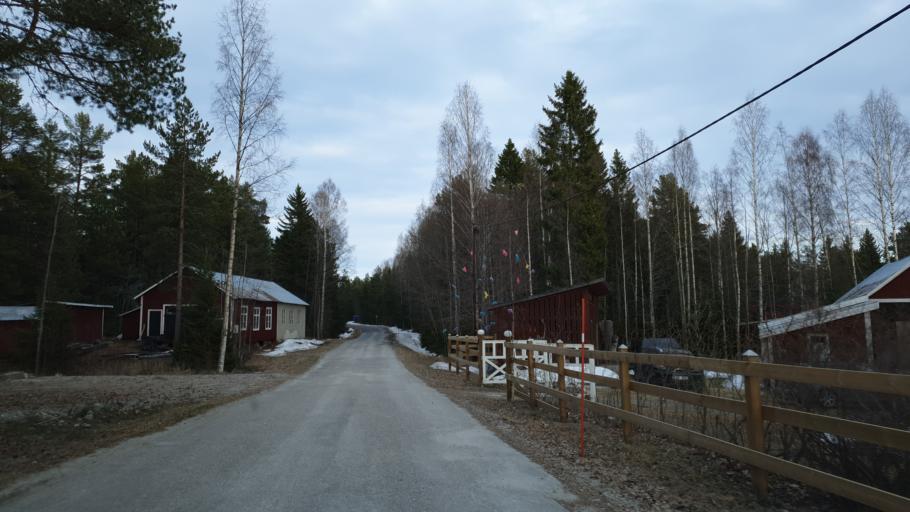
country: SE
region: Gaevleborg
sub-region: Nordanstigs Kommun
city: Bergsjoe
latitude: 61.9579
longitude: 17.3459
